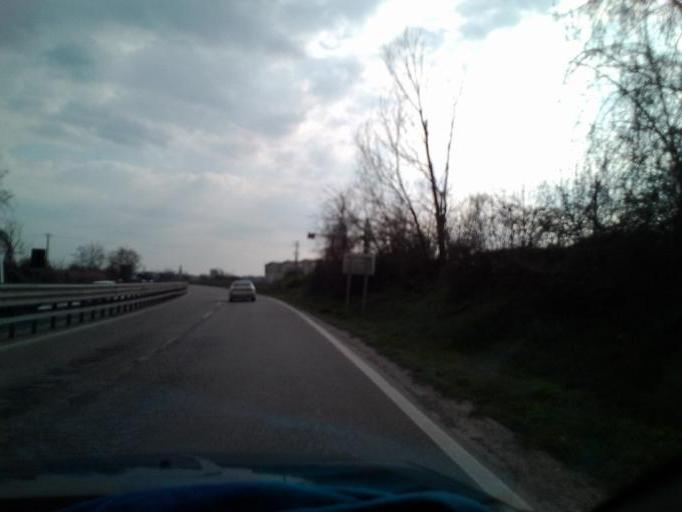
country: IT
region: Veneto
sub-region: Provincia di Verona
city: Pescantina
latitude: 45.4952
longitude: 10.8584
